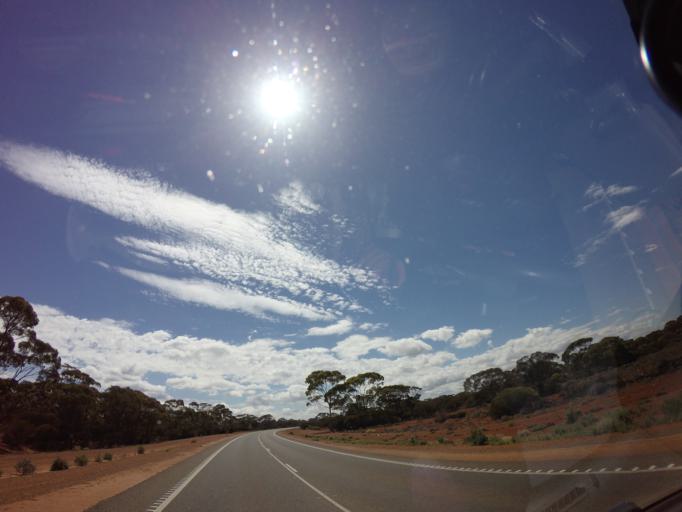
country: AU
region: Western Australia
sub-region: Kalgoorlie/Boulder
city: Boulder
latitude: -30.9551
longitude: 121.1371
